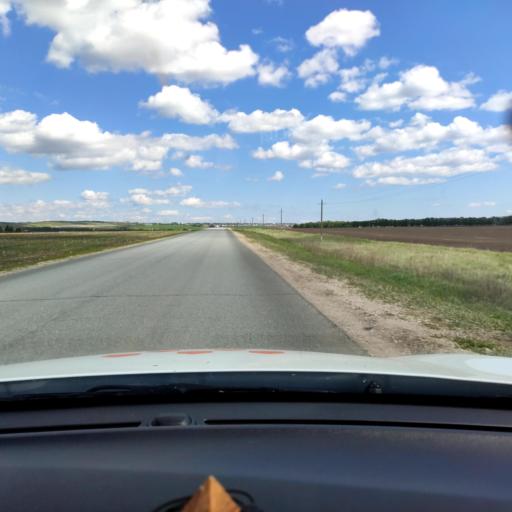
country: RU
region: Tatarstan
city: Kuybyshevskiy Zaton
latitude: 55.1641
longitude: 49.2021
